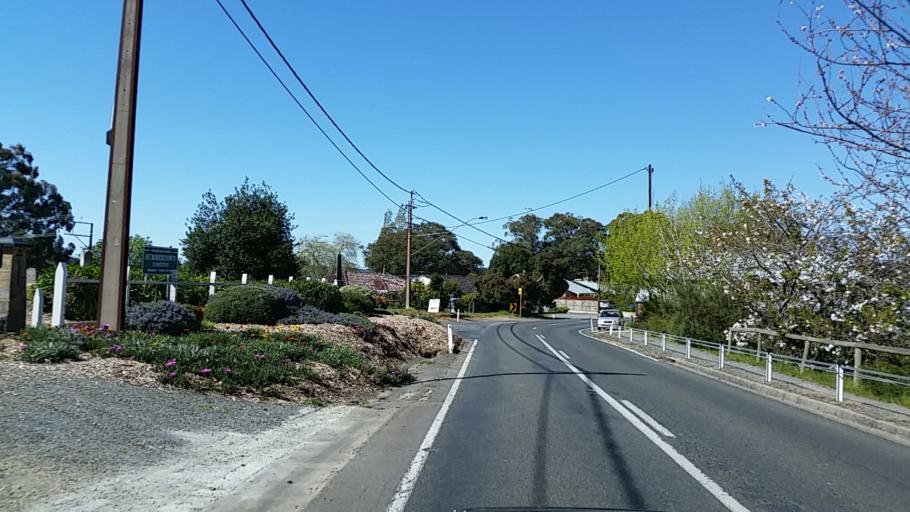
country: AU
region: South Australia
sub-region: Adelaide Hills
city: Bridgewater
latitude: -34.9588
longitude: 138.7363
